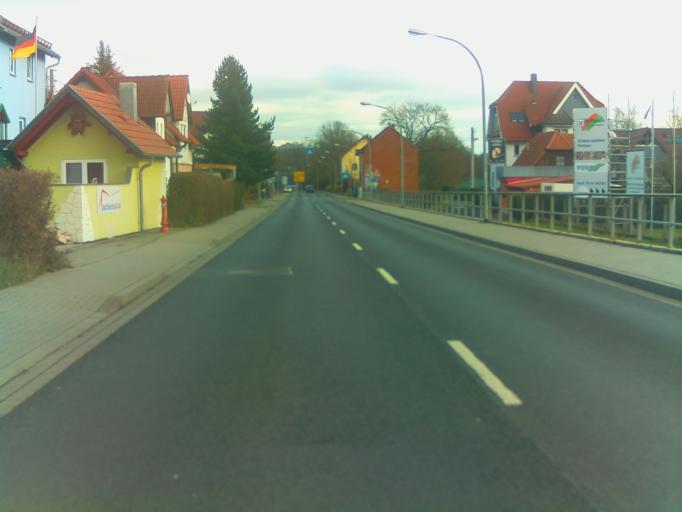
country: DE
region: Thuringia
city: Hildburghausen
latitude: 50.4219
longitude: 10.7127
